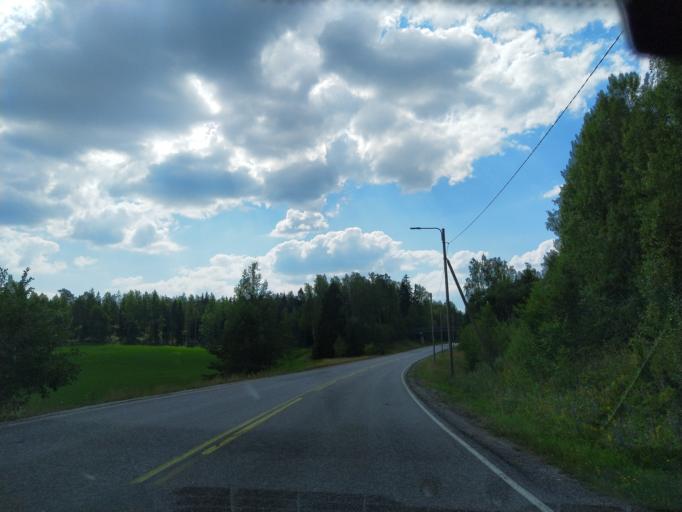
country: FI
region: Uusimaa
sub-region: Helsinki
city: Kirkkonummi
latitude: 60.1113
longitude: 24.4838
